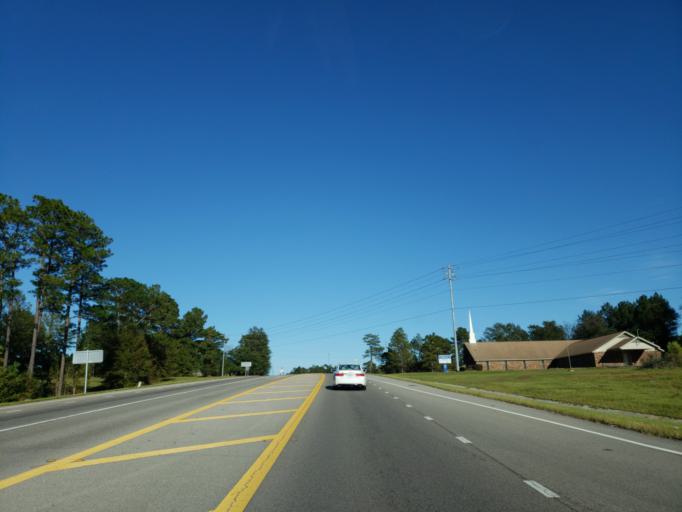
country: US
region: Mississippi
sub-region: Forrest County
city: Petal
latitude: 31.3518
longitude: -89.1753
